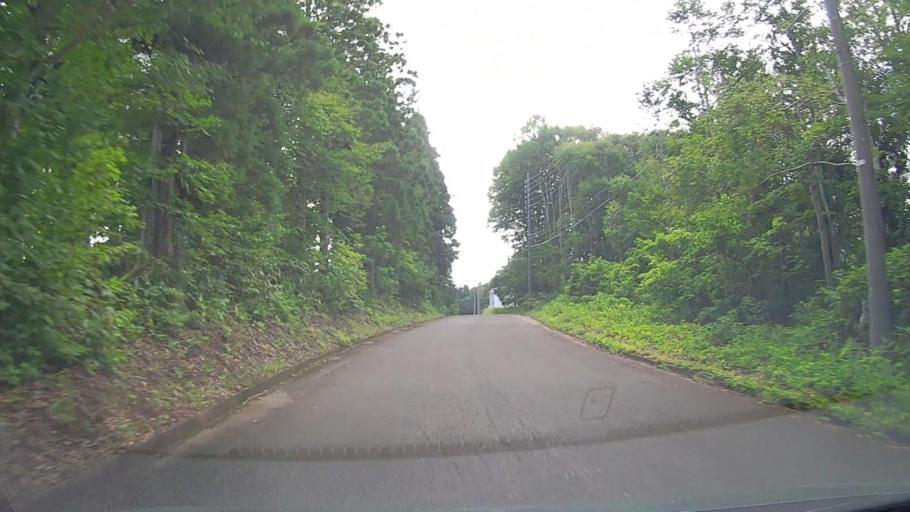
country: JP
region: Nagano
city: Iiyama
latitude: 36.9193
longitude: 138.4812
